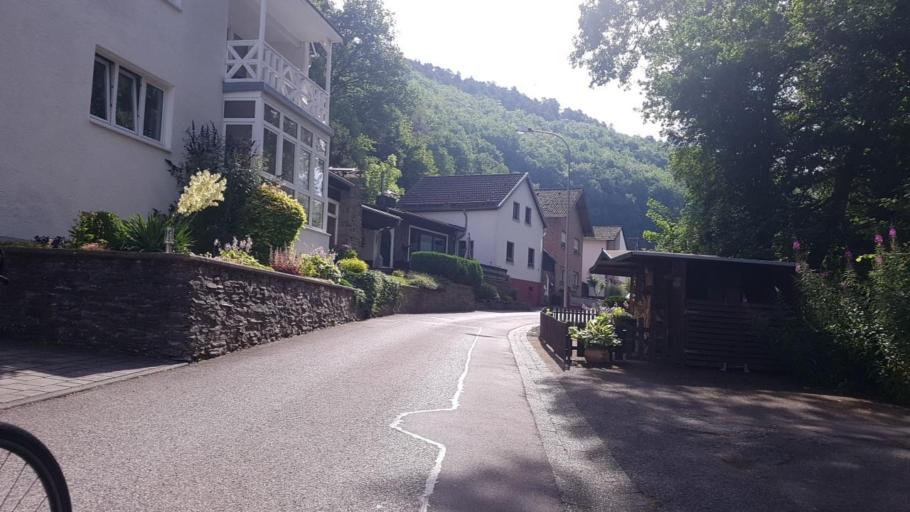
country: DE
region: North Rhine-Westphalia
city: Heimbach
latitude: 50.6295
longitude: 6.4910
